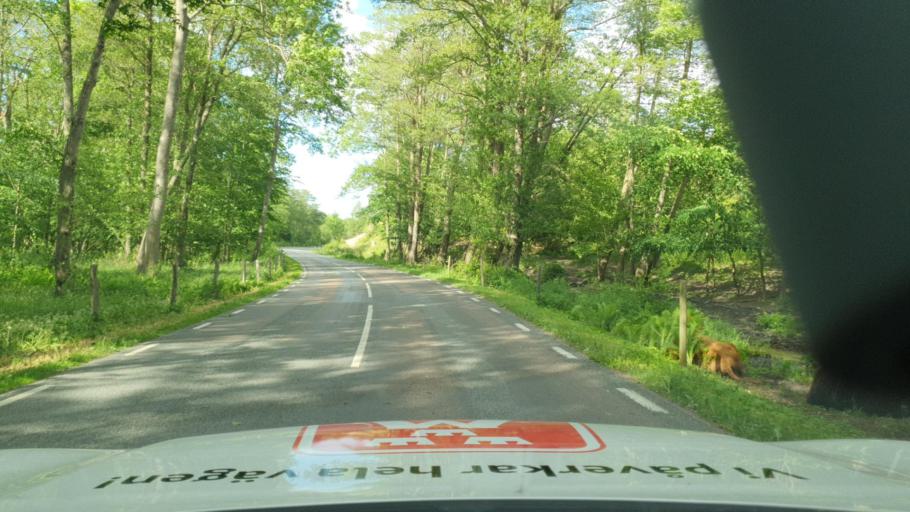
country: SE
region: Skane
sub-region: Simrishamns Kommun
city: Kivik
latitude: 55.6205
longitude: 14.2446
